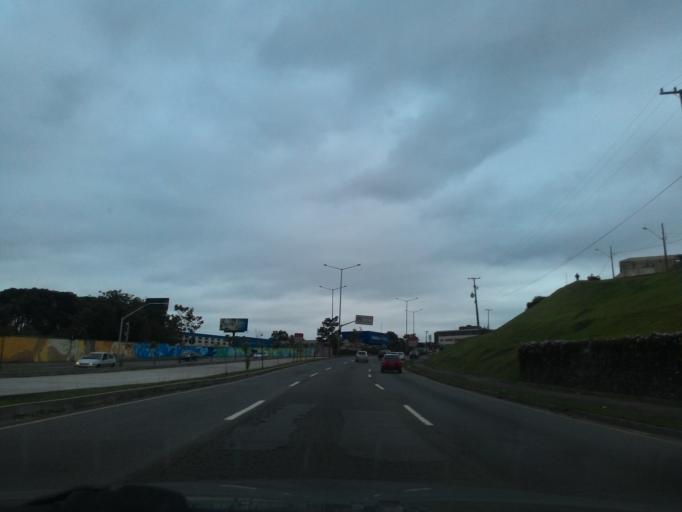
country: BR
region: Parana
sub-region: Curitiba
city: Curitiba
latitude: -25.4565
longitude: -49.2487
